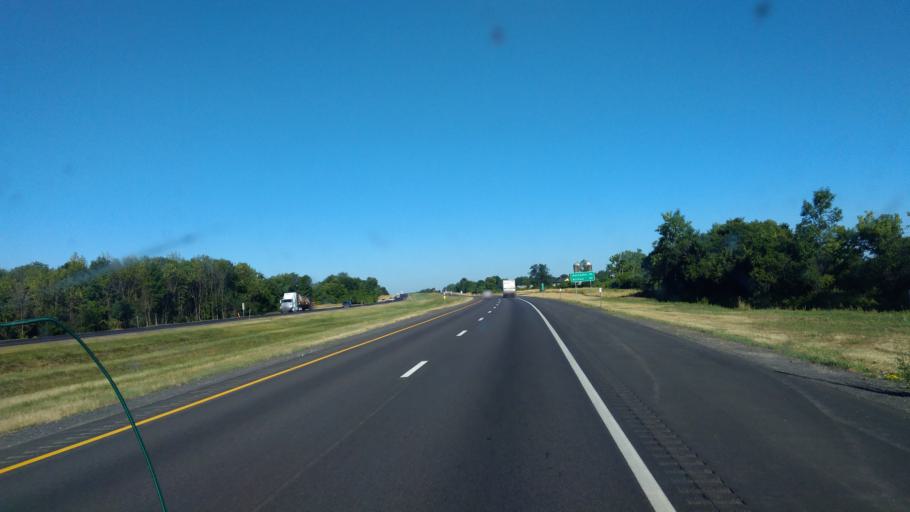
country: US
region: New York
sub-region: Ontario County
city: Phelps
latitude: 42.9742
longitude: -77.0907
